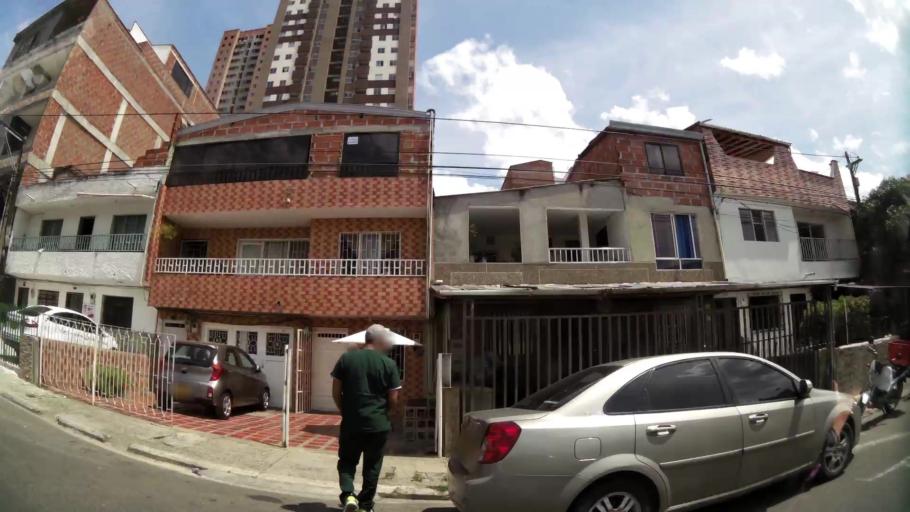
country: CO
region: Antioquia
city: Bello
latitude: 6.3414
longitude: -75.5518
